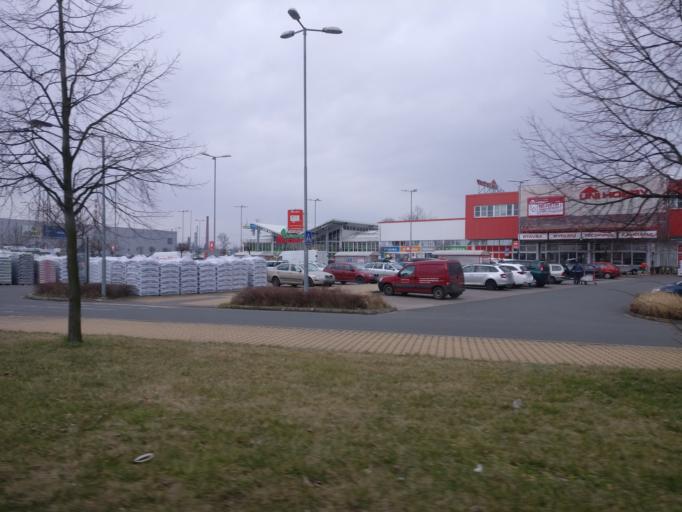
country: CZ
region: Pardubicky
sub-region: Okres Pardubice
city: Pardubice
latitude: 50.0362
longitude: 15.7540
